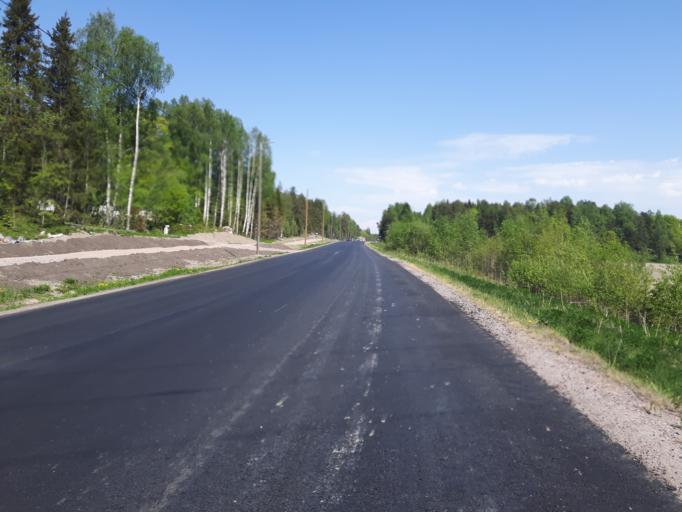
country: FI
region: Uusimaa
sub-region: Porvoo
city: Porvoo
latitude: 60.3593
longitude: 25.5359
